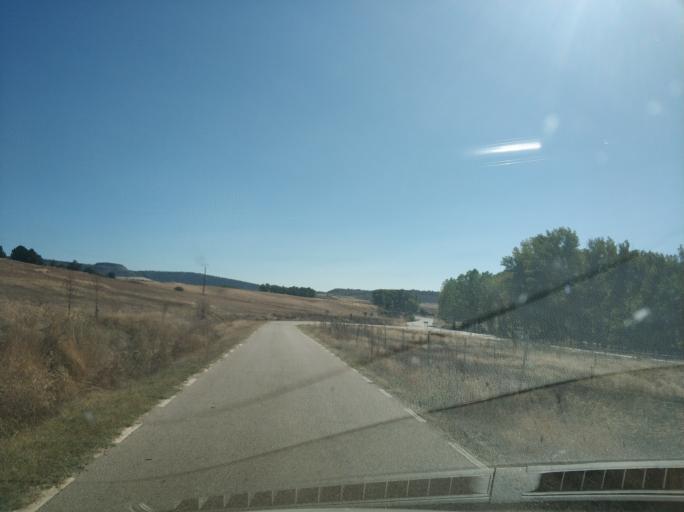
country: ES
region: Castille and Leon
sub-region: Provincia de Soria
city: Santa Maria de las Hoyas
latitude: 41.7703
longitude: -3.1677
